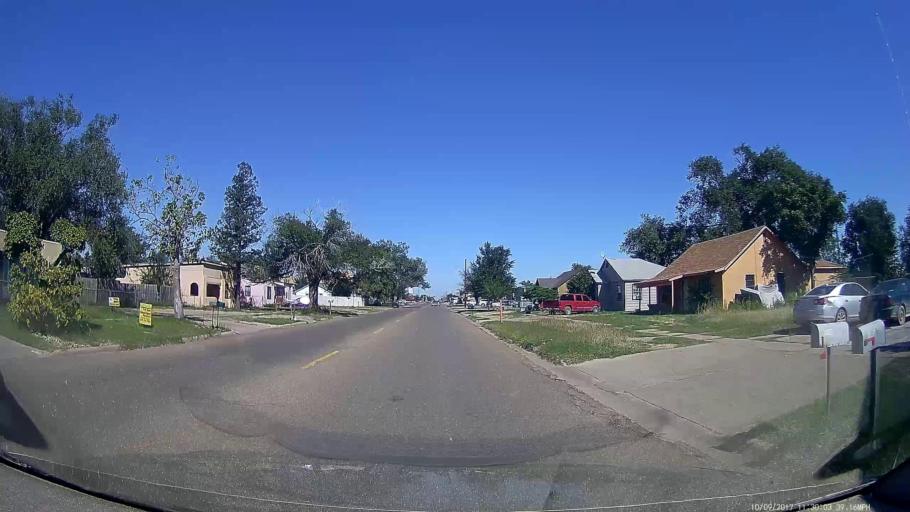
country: US
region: New Mexico
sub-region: Curry County
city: Clovis
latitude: 34.4084
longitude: -103.2142
